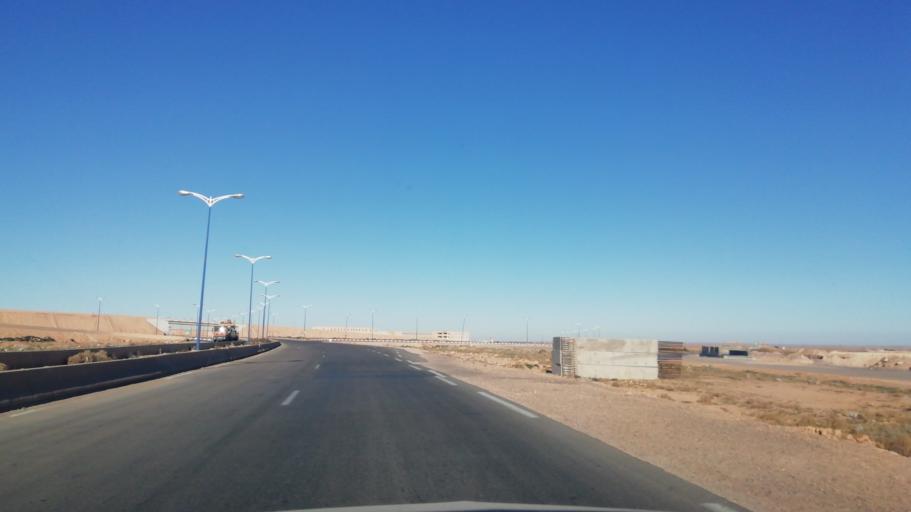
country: DZ
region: Wilaya de Naama
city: Naama
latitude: 33.5537
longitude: -0.2384
